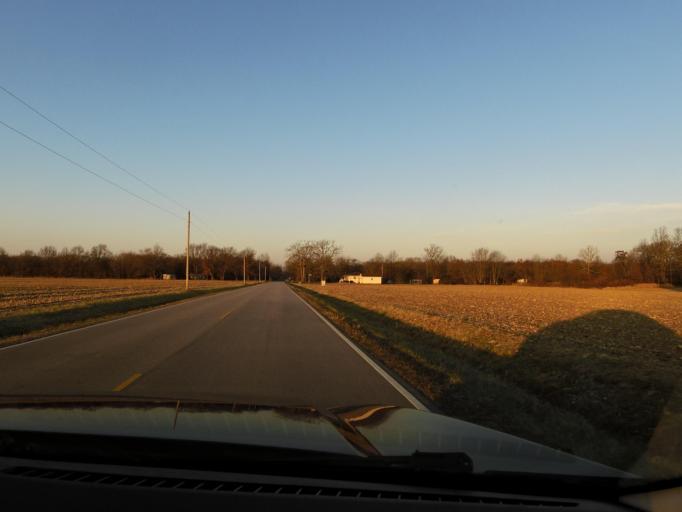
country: US
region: Illinois
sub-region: Marion County
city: Salem
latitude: 38.7587
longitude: -88.9229
